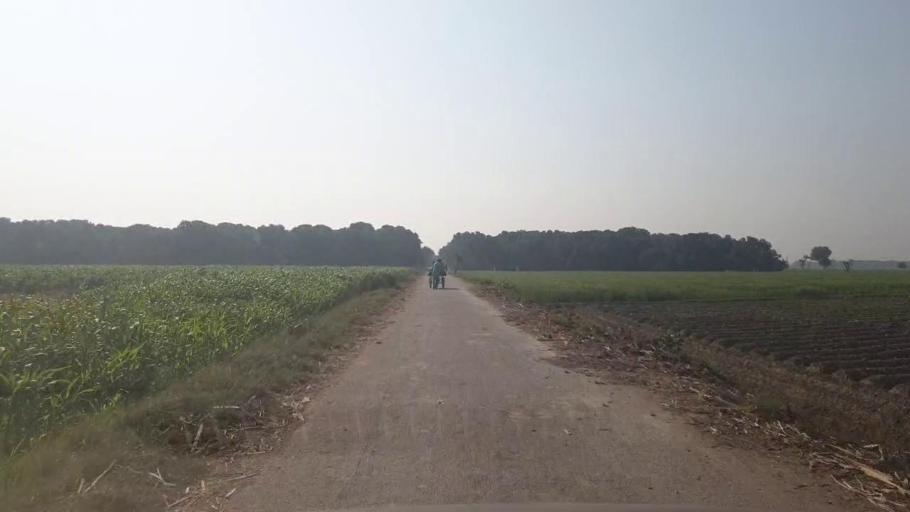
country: PK
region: Sindh
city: Tando Allahyar
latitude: 25.4731
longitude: 68.7620
